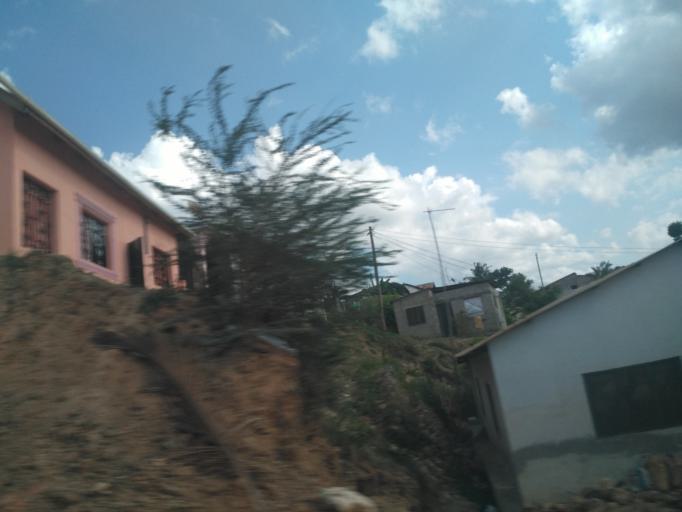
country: TZ
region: Dar es Salaam
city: Dar es Salaam
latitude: -6.8949
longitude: 39.2769
